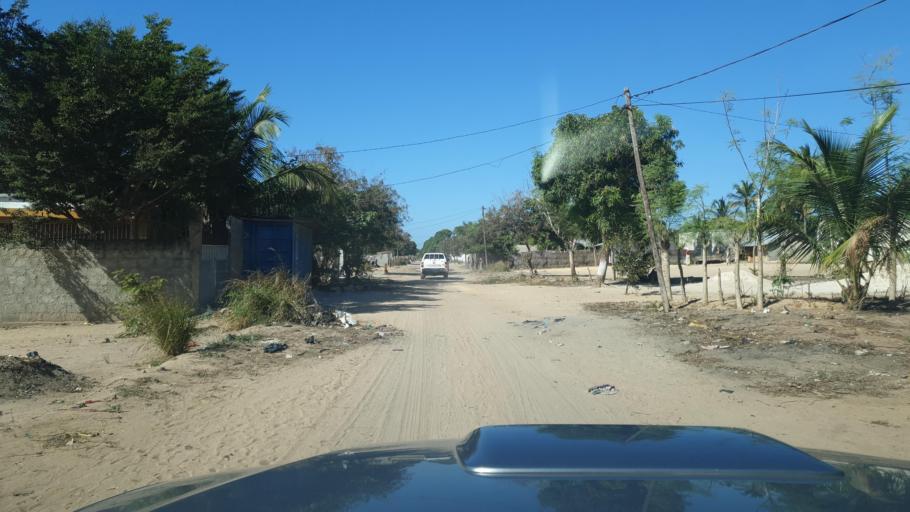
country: MZ
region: Nampula
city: Nacala
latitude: -14.5333
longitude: 40.7020
